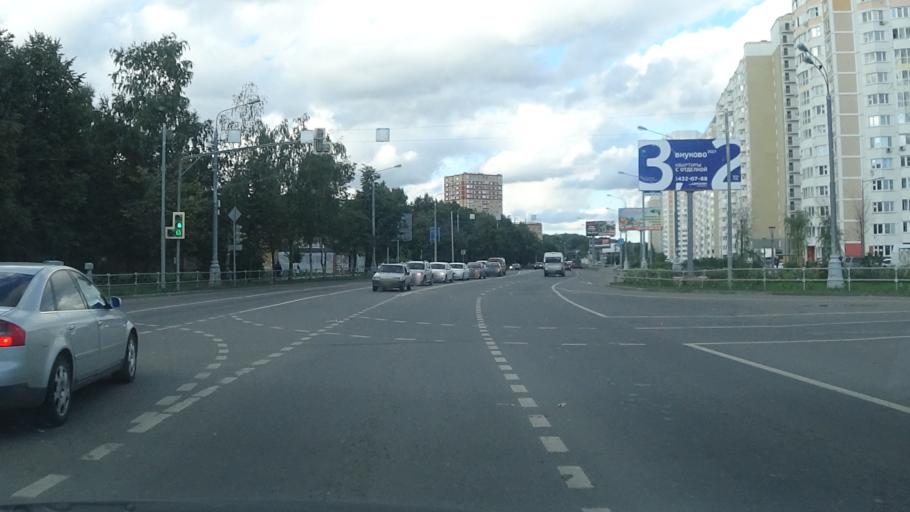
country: RU
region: Moskovskaya
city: Moskovskiy
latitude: 55.5990
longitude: 37.3552
